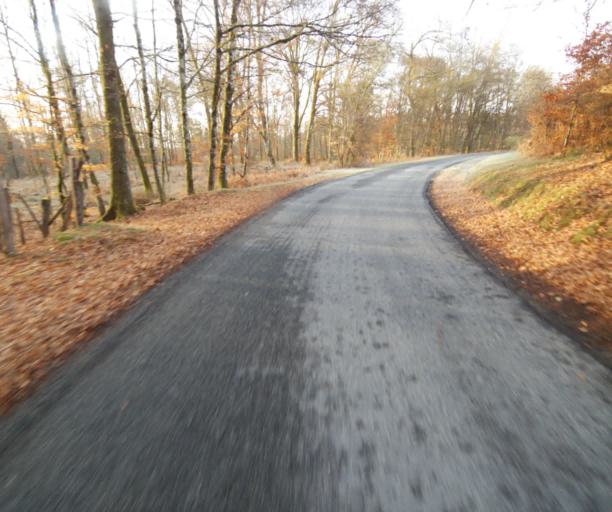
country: FR
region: Limousin
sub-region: Departement de la Correze
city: Correze
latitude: 45.3168
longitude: 1.8604
